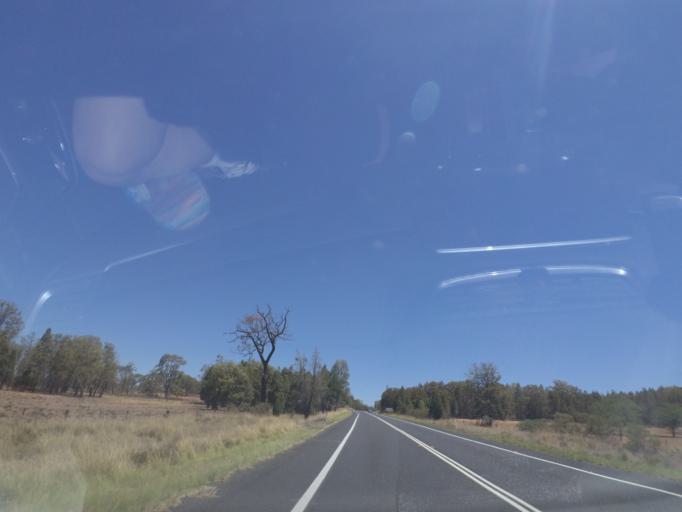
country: AU
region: New South Wales
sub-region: Warrumbungle Shire
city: Coonabarabran
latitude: -31.3731
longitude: 149.2679
